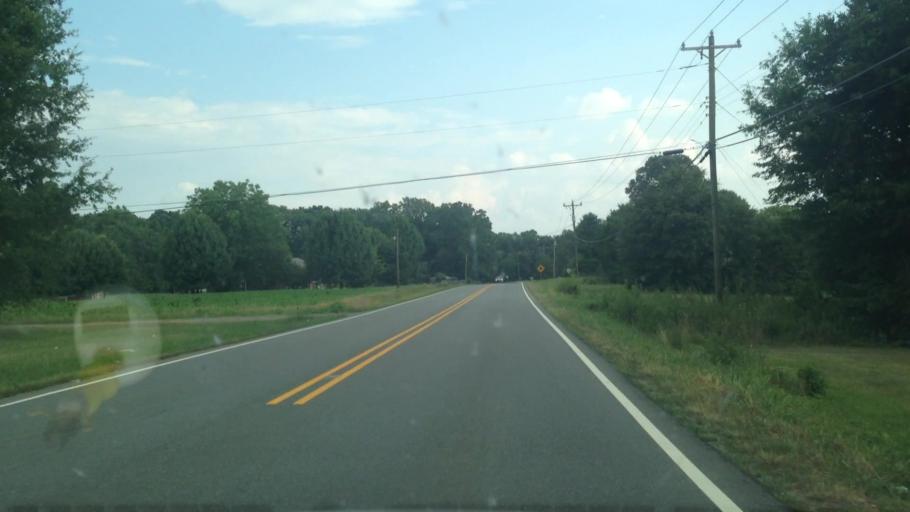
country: US
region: North Carolina
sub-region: Forsyth County
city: Walkertown
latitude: 36.1482
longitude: -80.1278
